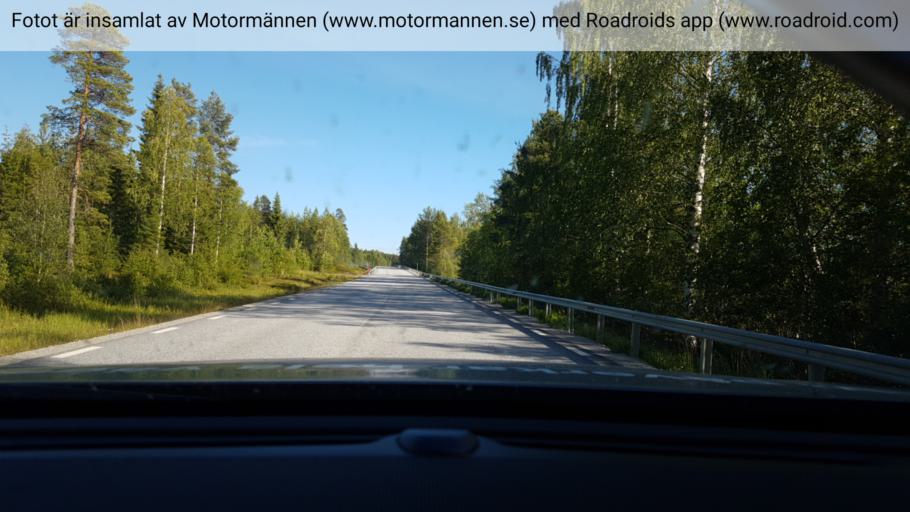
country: SE
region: Vaesterbotten
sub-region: Vindelns Kommun
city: Vindeln
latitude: 64.1881
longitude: 19.4659
